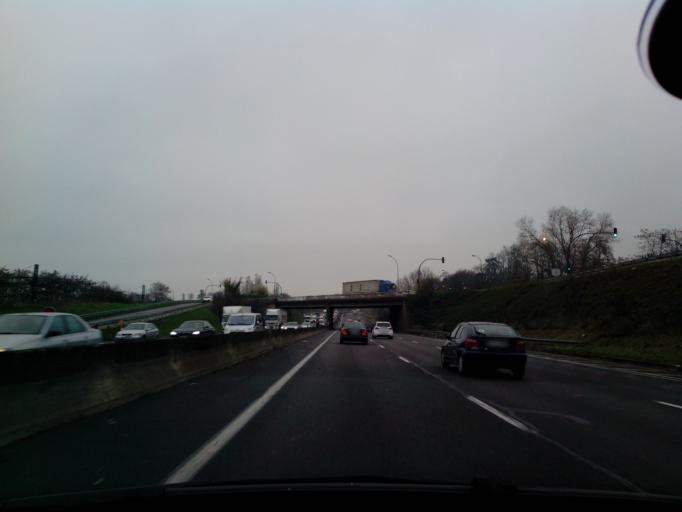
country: FR
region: Ile-de-France
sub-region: Departement de l'Essonne
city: Longjumeau
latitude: 48.6986
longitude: 2.3133
